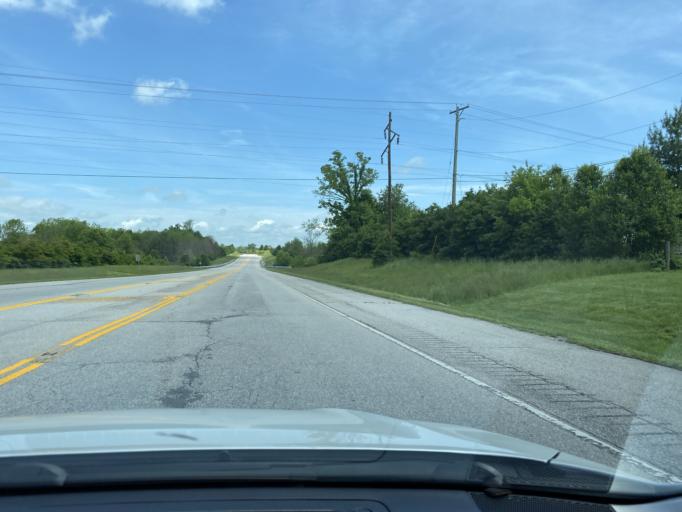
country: US
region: Kentucky
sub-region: Scott County
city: Georgetown
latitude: 38.2315
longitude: -84.5473
